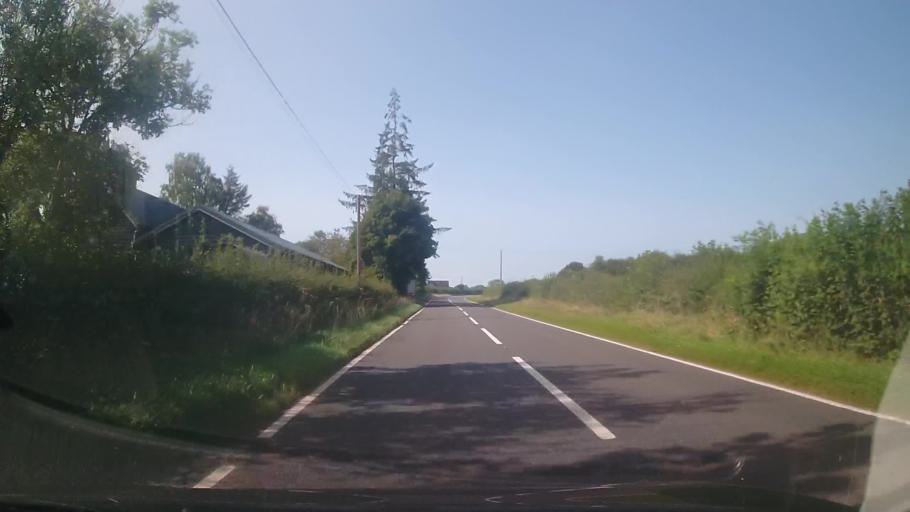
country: GB
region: Wales
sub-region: Sir Powys
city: Builth Wells
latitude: 52.1393
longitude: -3.5093
